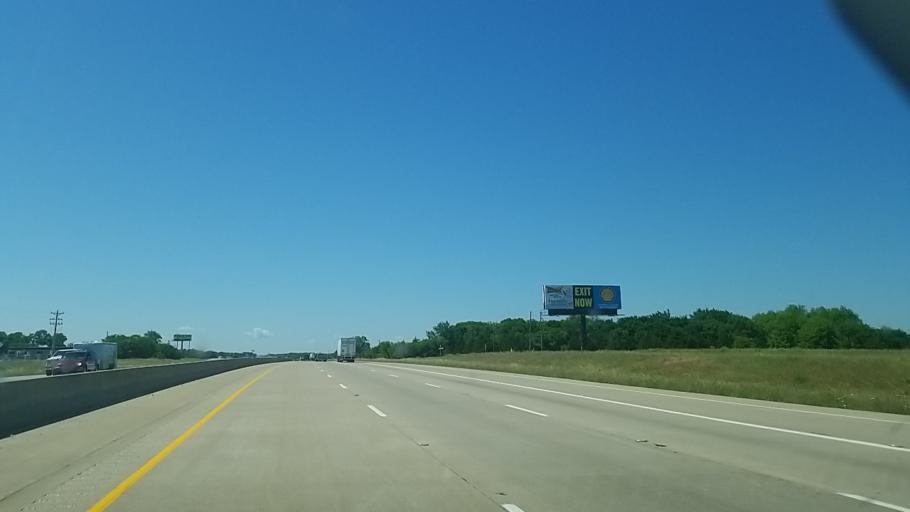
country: US
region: Texas
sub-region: Navarro County
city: Corsicana
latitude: 32.2215
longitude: -96.4848
